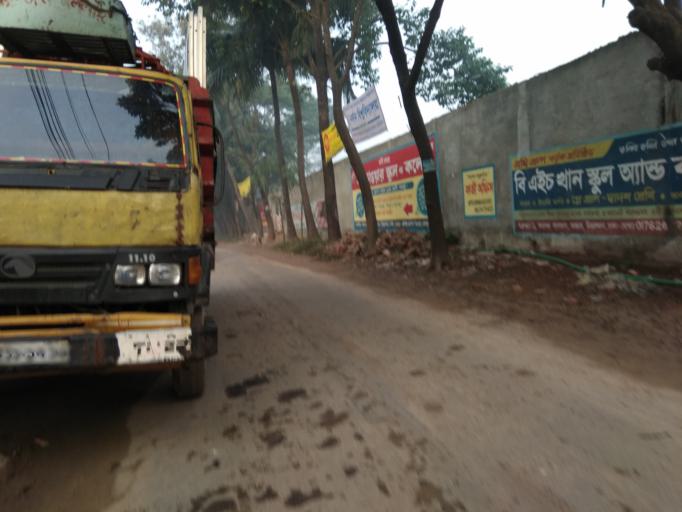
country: BD
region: Dhaka
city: Tungi
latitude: 23.8619
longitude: 90.4458
